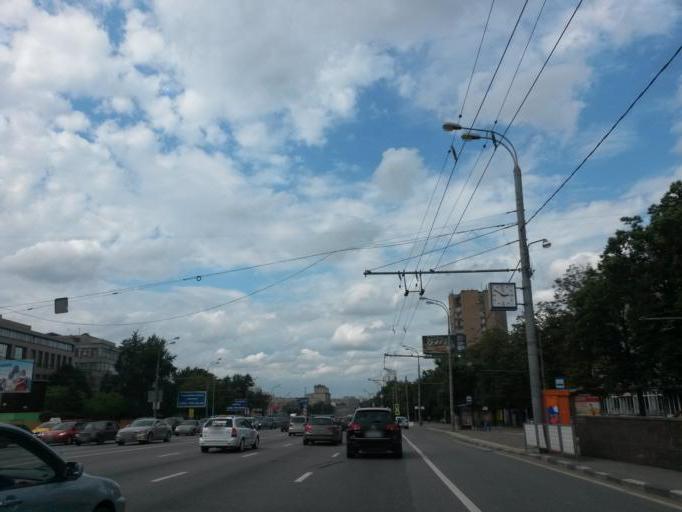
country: RU
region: Moscow
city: Kotlovka
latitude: 55.6840
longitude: 37.6235
